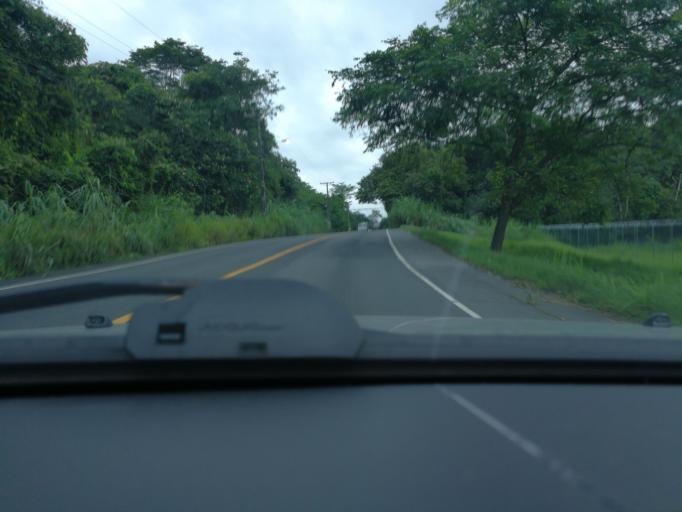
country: PA
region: Panama
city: Panama
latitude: 9.0059
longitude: -79.5456
